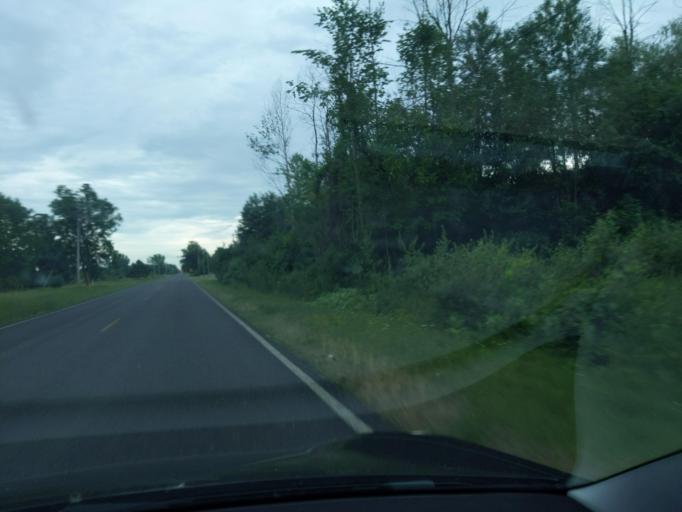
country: US
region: Michigan
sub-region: Isabella County
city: Mount Pleasant
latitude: 43.6158
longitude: -84.7278
